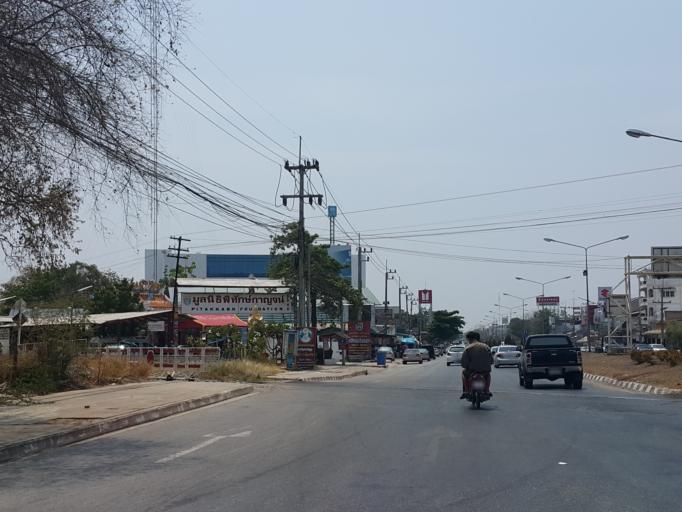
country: TH
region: Kanchanaburi
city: Kanchanaburi
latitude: 14.0464
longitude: 99.5095
